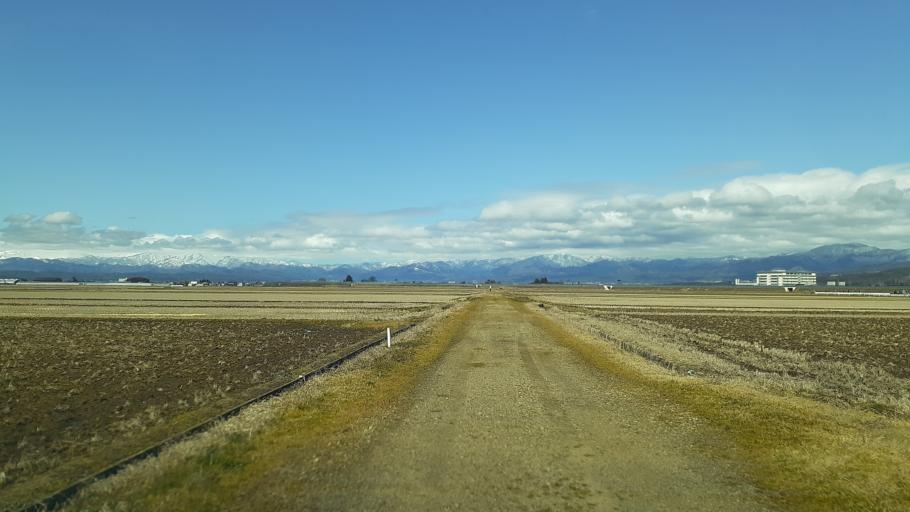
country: JP
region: Fukushima
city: Kitakata
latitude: 37.5421
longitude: 139.9033
